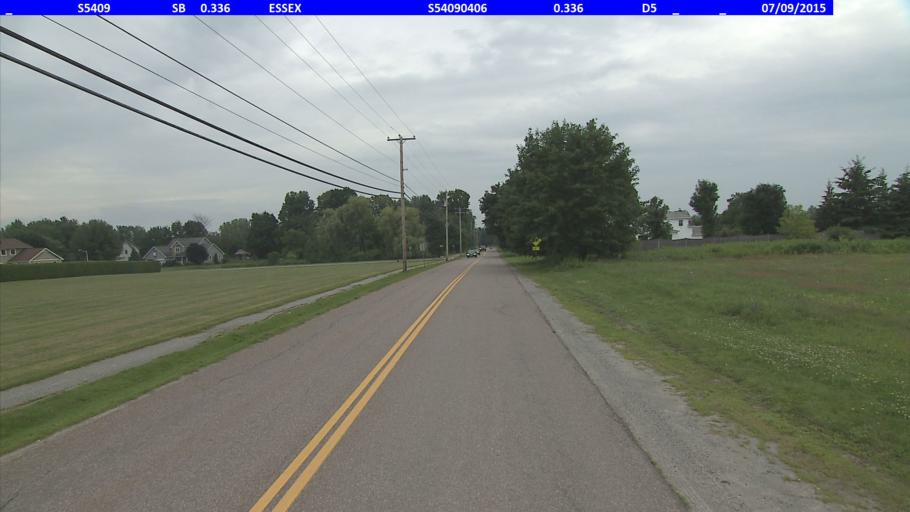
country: US
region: Vermont
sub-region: Chittenden County
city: Essex Junction
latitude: 44.5148
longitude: -73.0822
